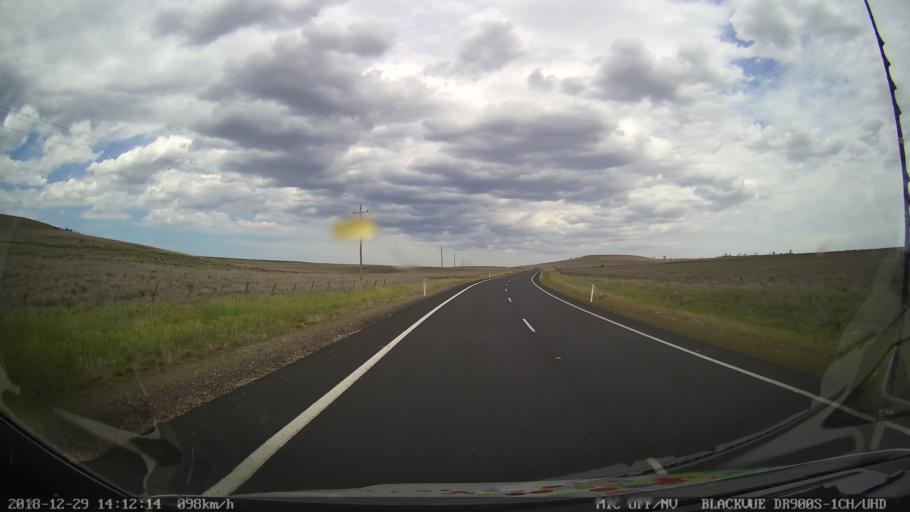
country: AU
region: New South Wales
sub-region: Cooma-Monaro
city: Cooma
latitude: -36.4132
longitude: 149.2301
